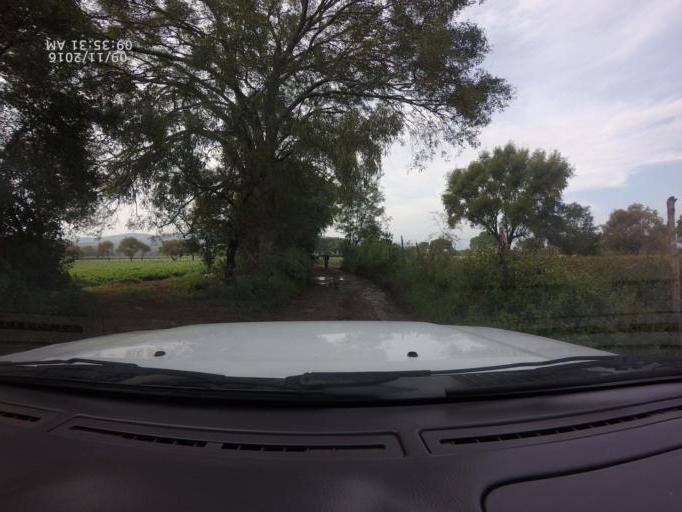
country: MX
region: Michoacan
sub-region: Morelia
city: La Mintzita (Piedra Dura)
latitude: 19.5729
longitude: -101.2900
